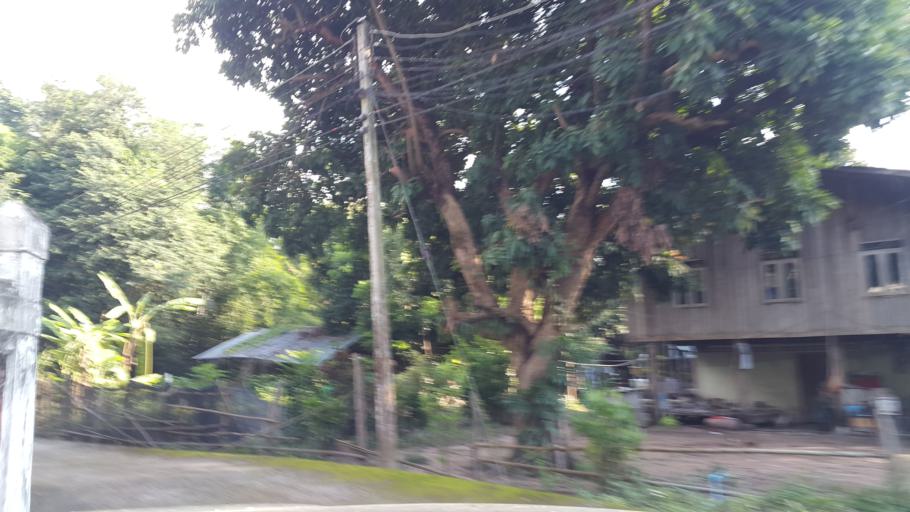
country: TH
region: Chiang Mai
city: Mae On
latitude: 18.7194
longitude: 99.2092
